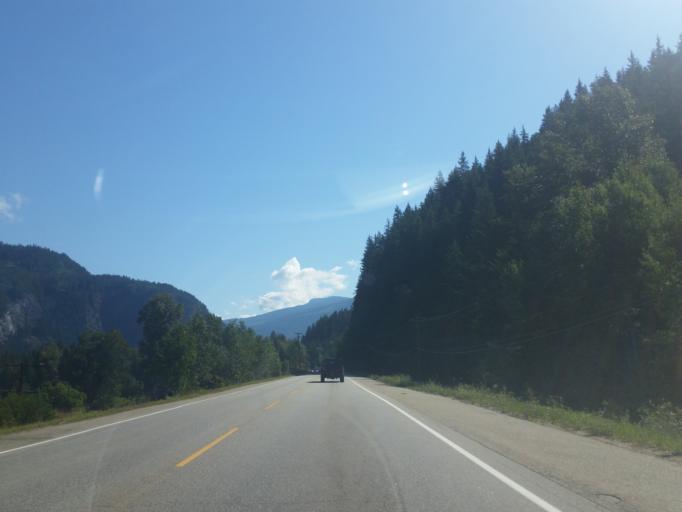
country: CA
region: British Columbia
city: Sicamous
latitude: 50.8863
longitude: -118.8939
